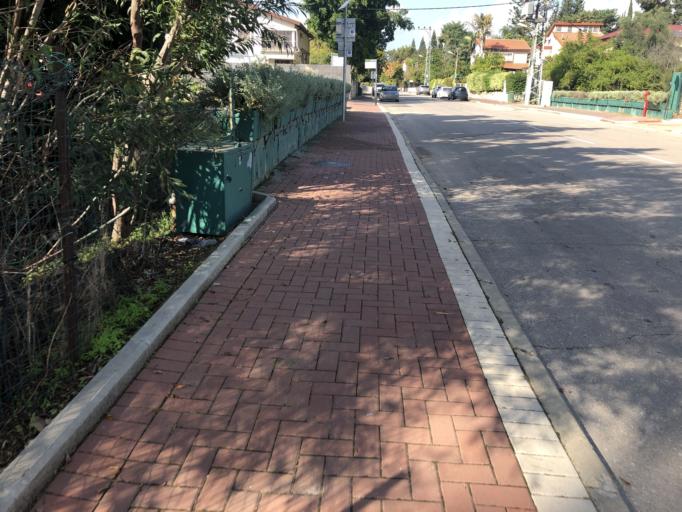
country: IL
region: Tel Aviv
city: Or Yehuda
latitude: 32.0310
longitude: 34.8740
